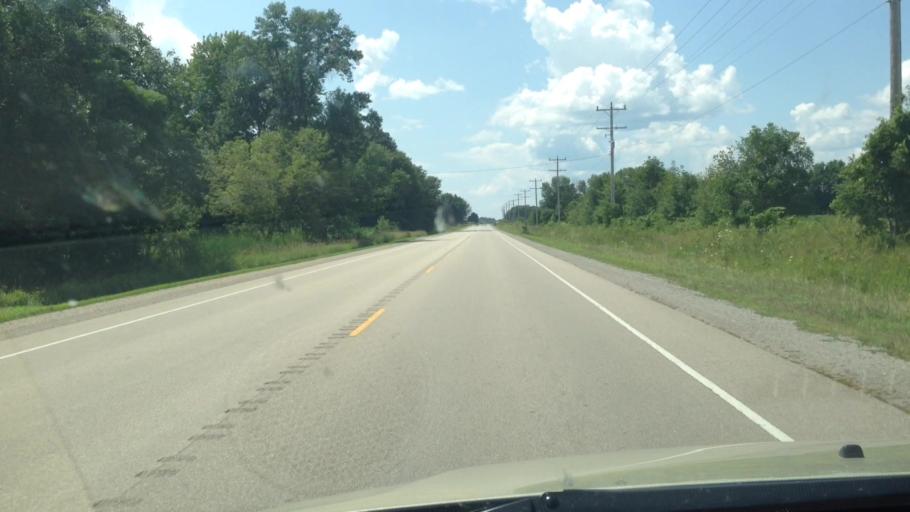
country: US
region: Wisconsin
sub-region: Brown County
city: Pulaski
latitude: 44.6734
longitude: -88.2837
